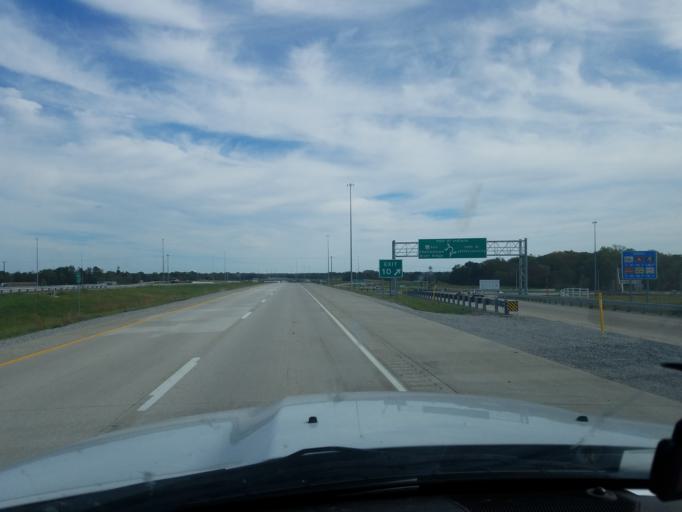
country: US
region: Indiana
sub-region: Clark County
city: Oak Park
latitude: 38.3440
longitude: -85.7100
